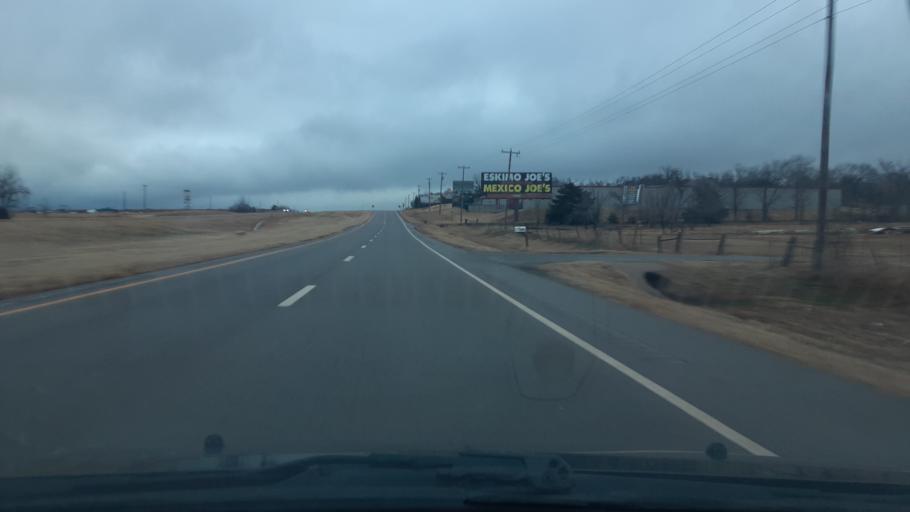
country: US
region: Oklahoma
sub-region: Payne County
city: Stillwater
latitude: 36.1158
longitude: -97.1713
